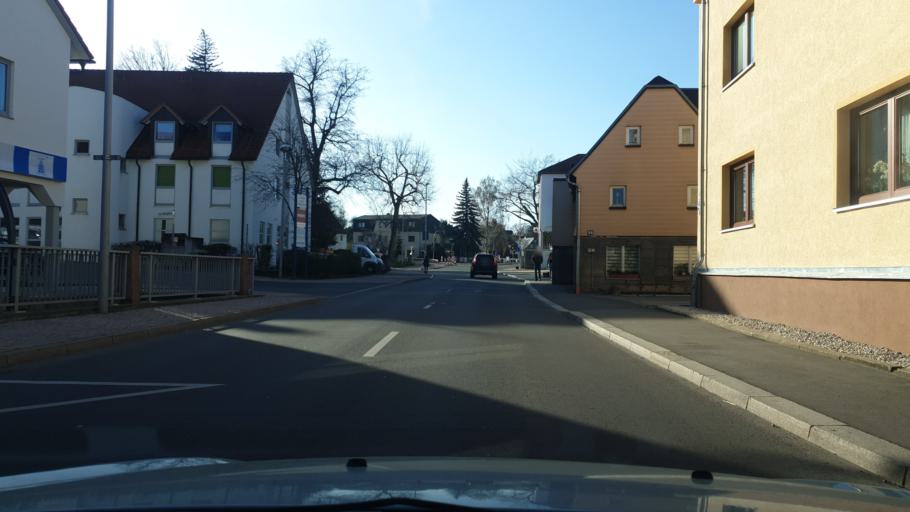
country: DE
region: Saxony
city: Neukirchen
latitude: 50.7787
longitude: 12.8685
